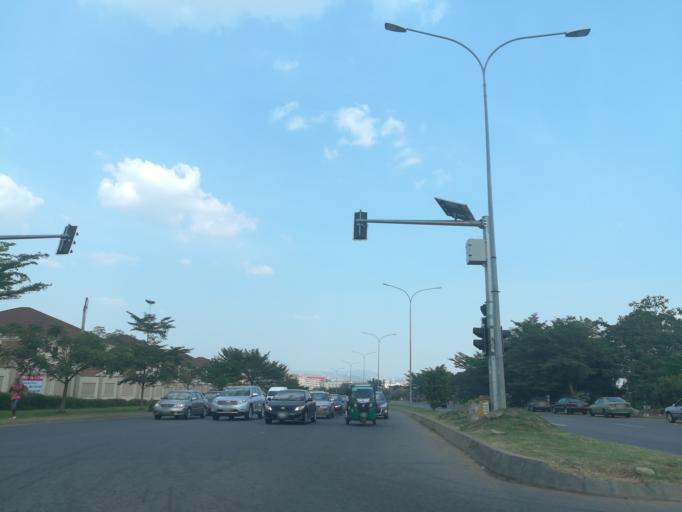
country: NG
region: Abuja Federal Capital Territory
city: Abuja
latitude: 9.0861
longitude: 7.4157
